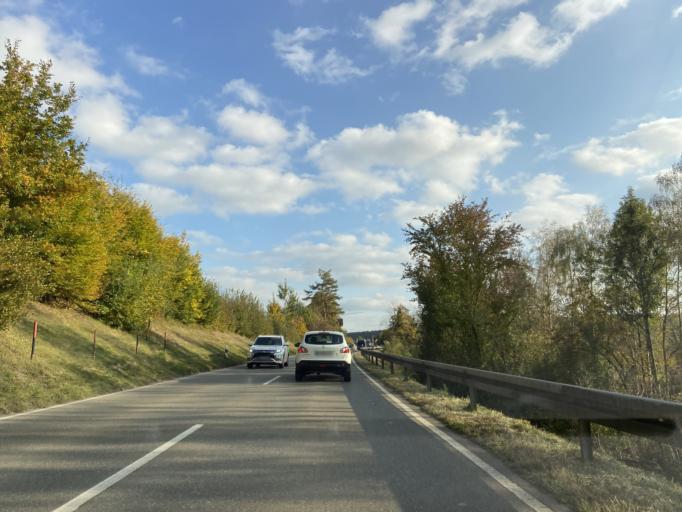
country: DE
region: Baden-Wuerttemberg
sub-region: Tuebingen Region
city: Sigmaringendorf
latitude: 48.0710
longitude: 9.2579
